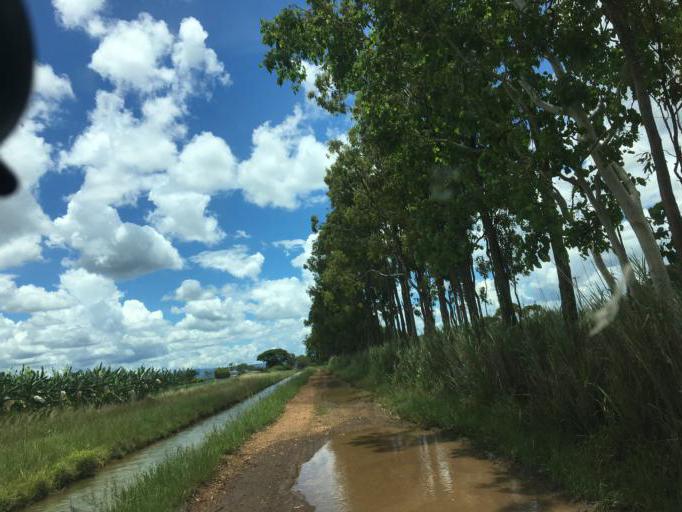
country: AU
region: Queensland
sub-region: Tablelands
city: Mareeba
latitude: -16.9889
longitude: 145.5254
